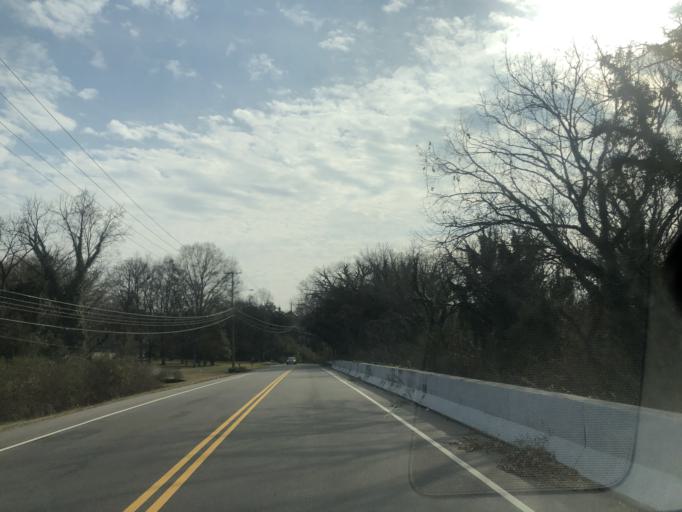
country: US
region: Tennessee
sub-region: Davidson County
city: Oak Hill
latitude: 36.1114
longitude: -86.7095
